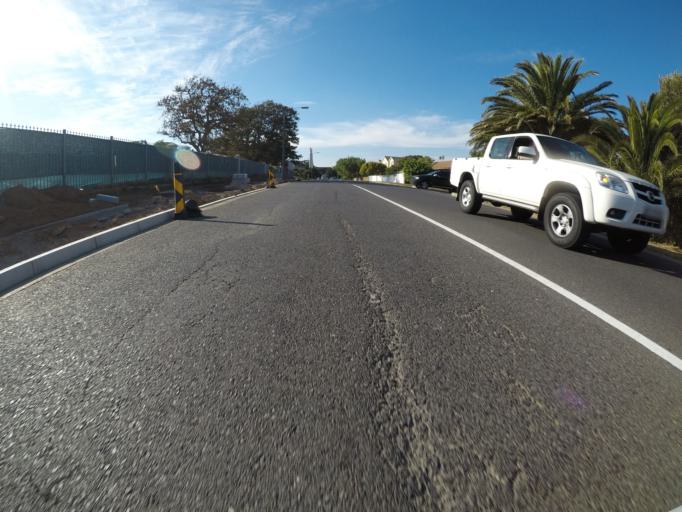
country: ZA
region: Western Cape
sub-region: City of Cape Town
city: Kraaifontein
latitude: -33.8769
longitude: 18.6457
